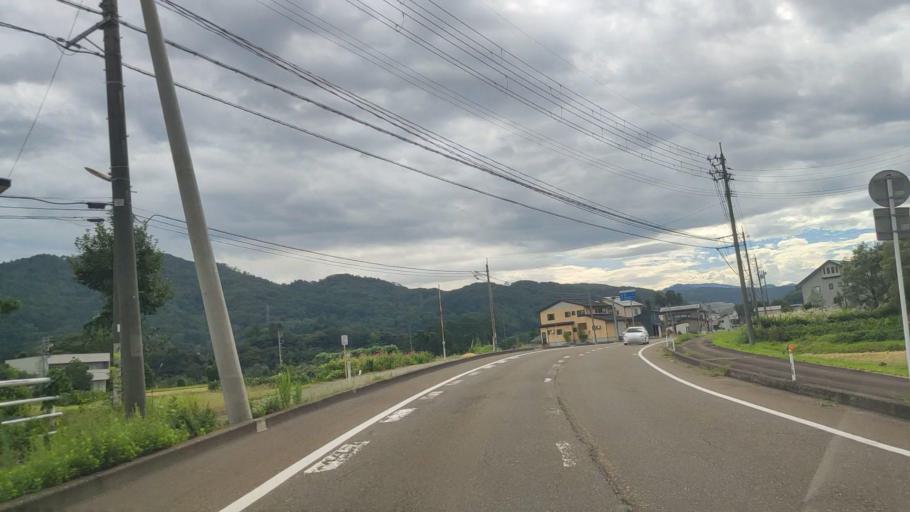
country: JP
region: Niigata
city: Arai
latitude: 37.0048
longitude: 138.2621
